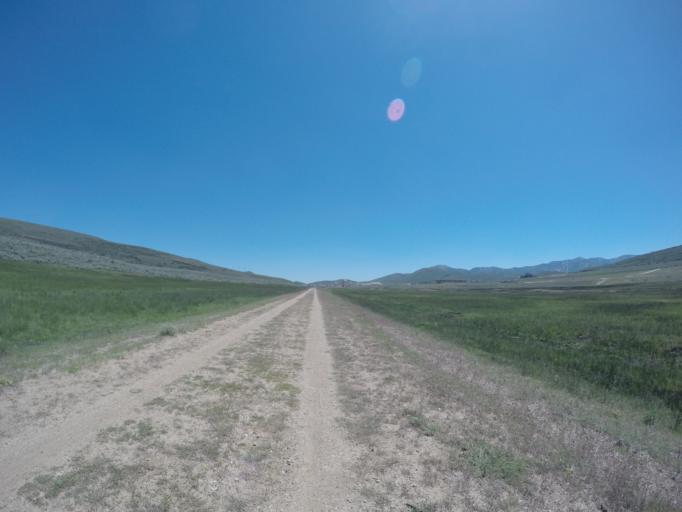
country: US
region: Utah
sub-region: Summit County
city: Park City
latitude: 40.6991
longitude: -111.4623
